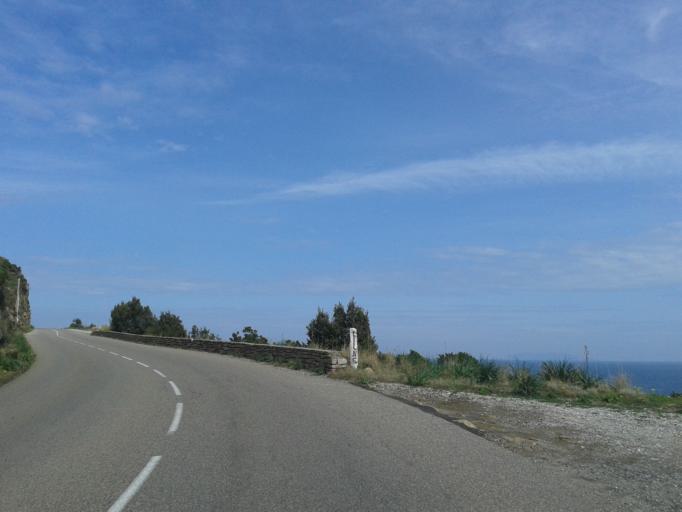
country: FR
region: Corsica
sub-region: Departement de la Haute-Corse
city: Brando
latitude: 42.7971
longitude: 9.4905
